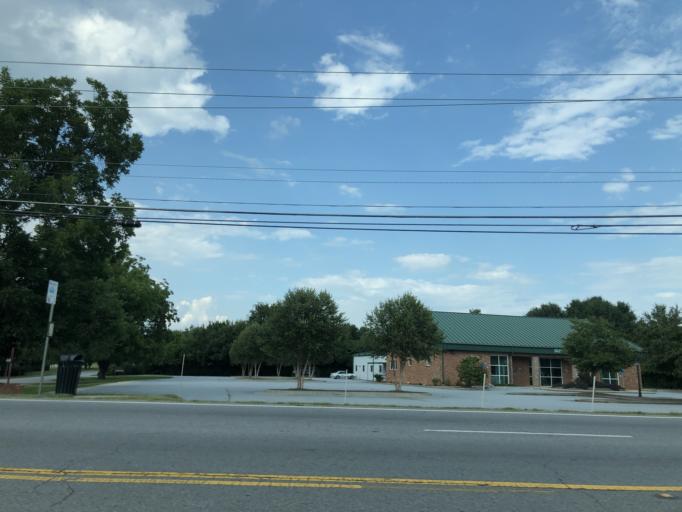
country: US
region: Georgia
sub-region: Clarke County
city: Athens
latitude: 33.9414
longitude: -83.3274
